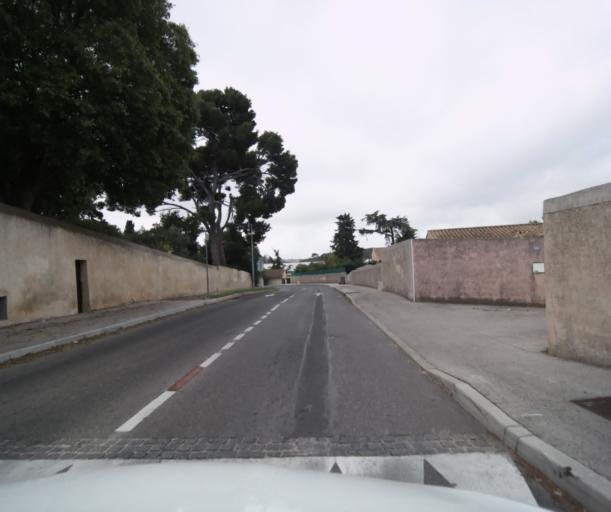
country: FR
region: Provence-Alpes-Cote d'Azur
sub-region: Departement du Var
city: La Seyne-sur-Mer
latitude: 43.1202
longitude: 5.8816
